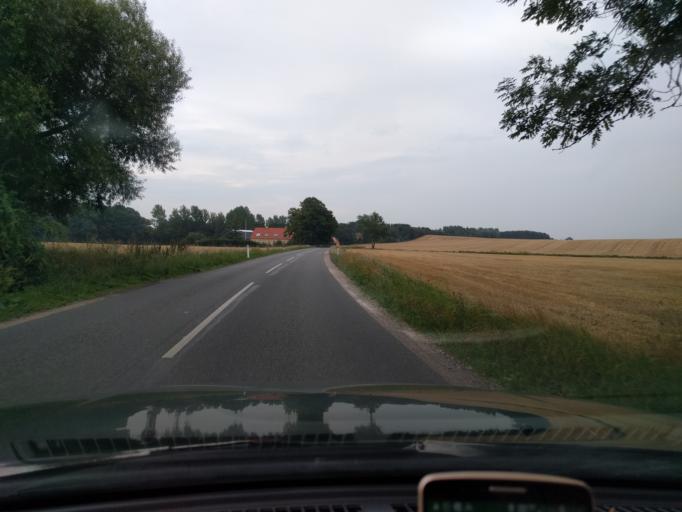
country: DK
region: Zealand
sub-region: Slagelse Kommune
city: Skaelskor
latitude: 55.2861
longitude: 11.2677
